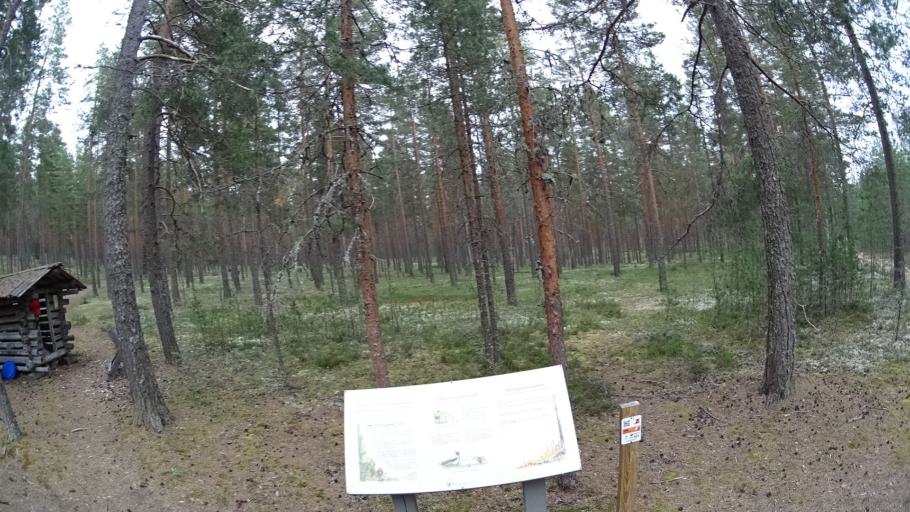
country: FI
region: Satakunta
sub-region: Pohjois-Satakunta
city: Jaemijaervi
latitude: 61.7679
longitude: 22.7493
